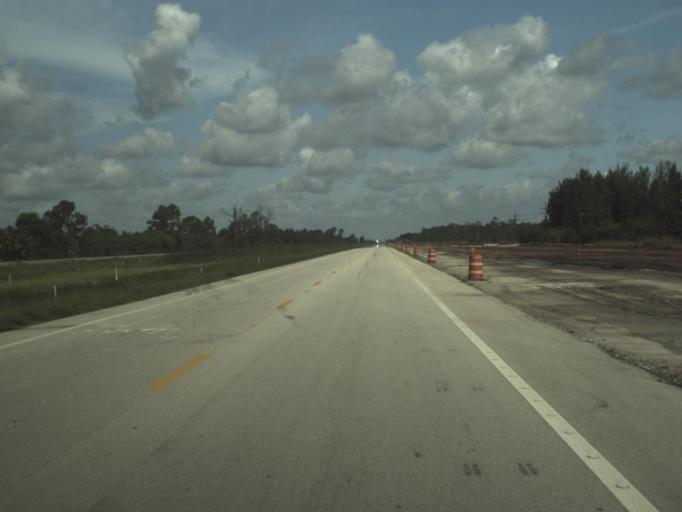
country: US
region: Florida
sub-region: Palm Beach County
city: Limestone Creek
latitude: 26.9250
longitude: -80.3247
